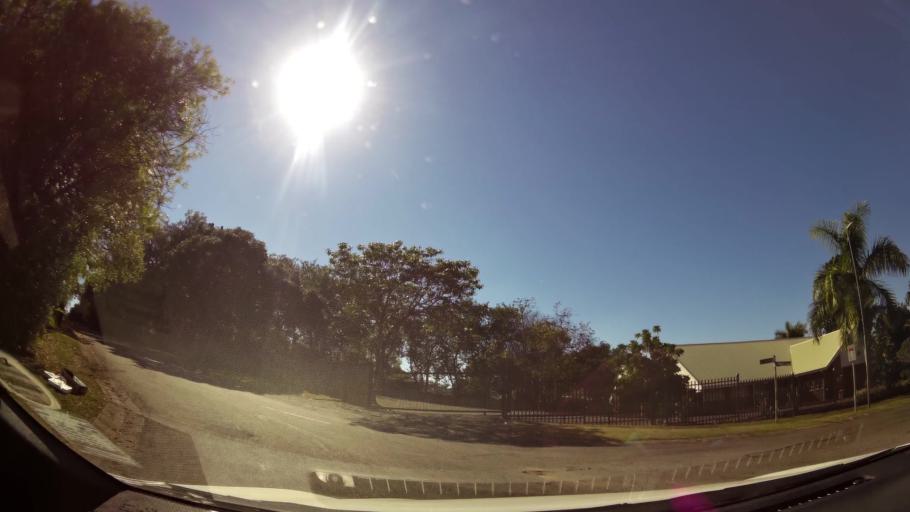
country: ZA
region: Limpopo
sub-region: Mopani District Municipality
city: Tzaneen
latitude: -23.8288
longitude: 30.1493
